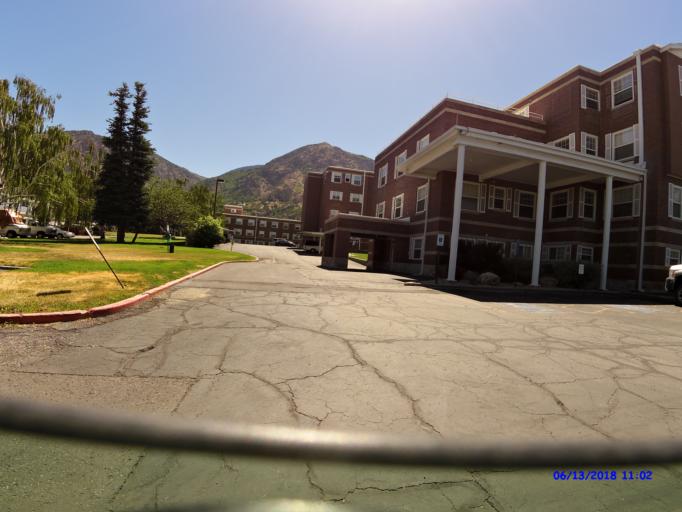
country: US
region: Utah
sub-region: Weber County
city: Ogden
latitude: 41.2103
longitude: -111.9425
